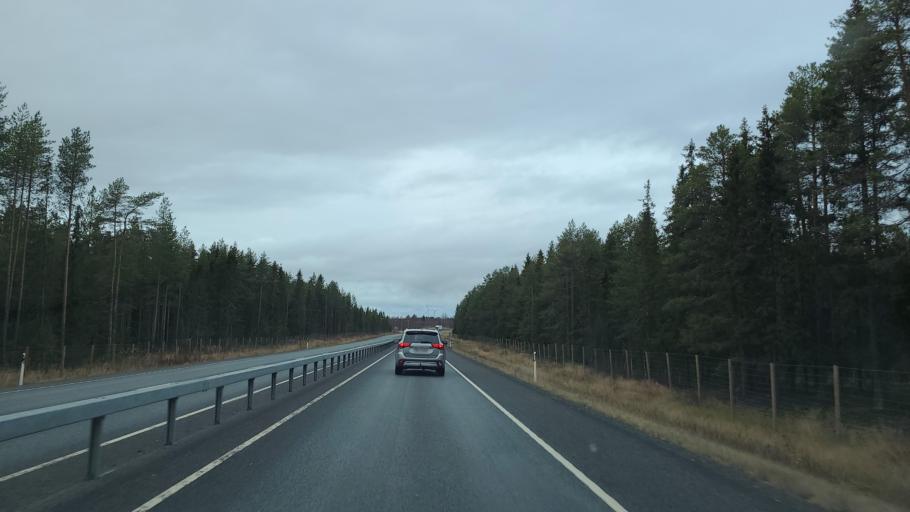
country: FI
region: Northern Ostrobothnia
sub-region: Oulunkaari
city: Kuivaniemi
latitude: 65.5750
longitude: 25.2096
